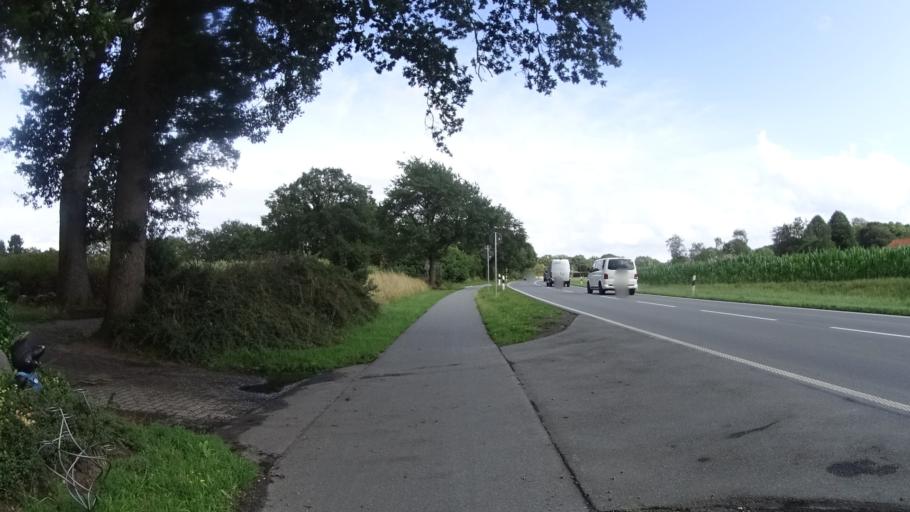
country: DE
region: Lower Saxony
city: Bockhorn
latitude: 53.3875
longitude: 8.0465
